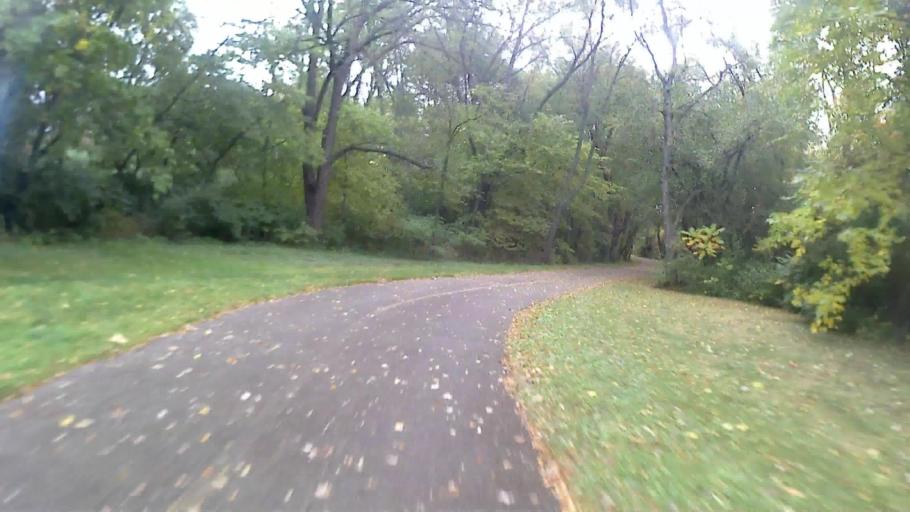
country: US
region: Illinois
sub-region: Kane County
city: Montgomery
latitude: 41.7507
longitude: -88.3751
